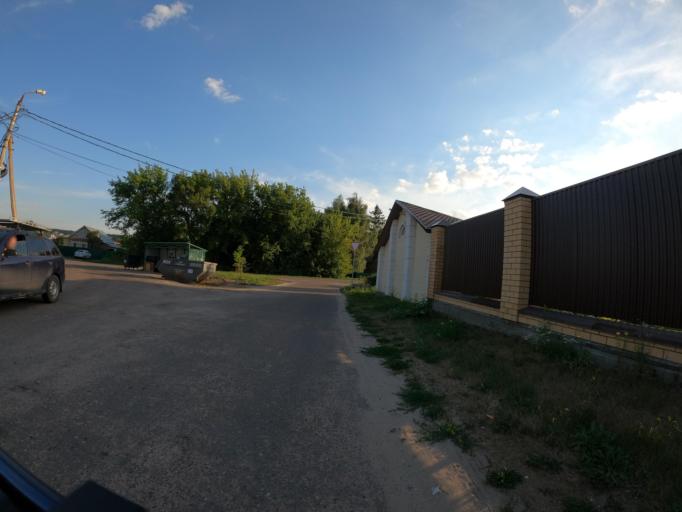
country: RU
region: Moskovskaya
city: Raduzhnyy
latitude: 55.1009
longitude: 38.7240
